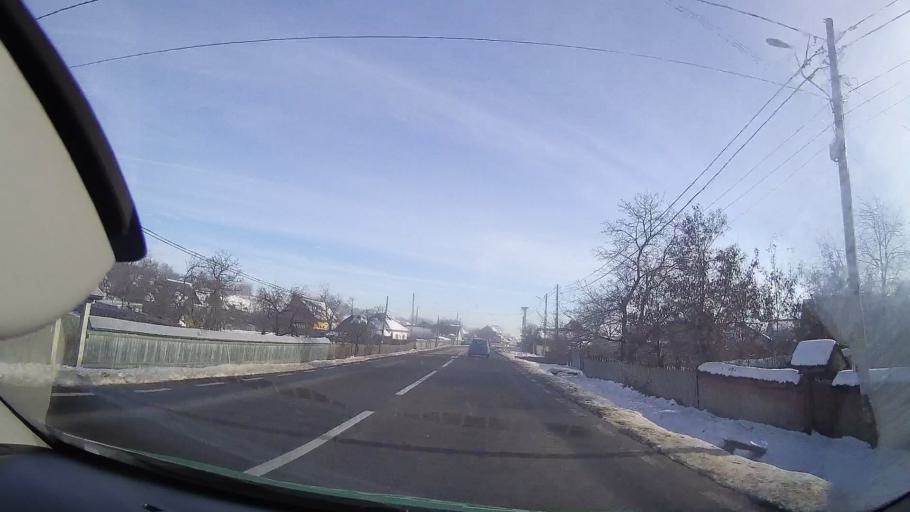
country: RO
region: Neamt
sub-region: Comuna Cracaoani
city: Cracaoani
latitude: 47.0885
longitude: 26.3283
